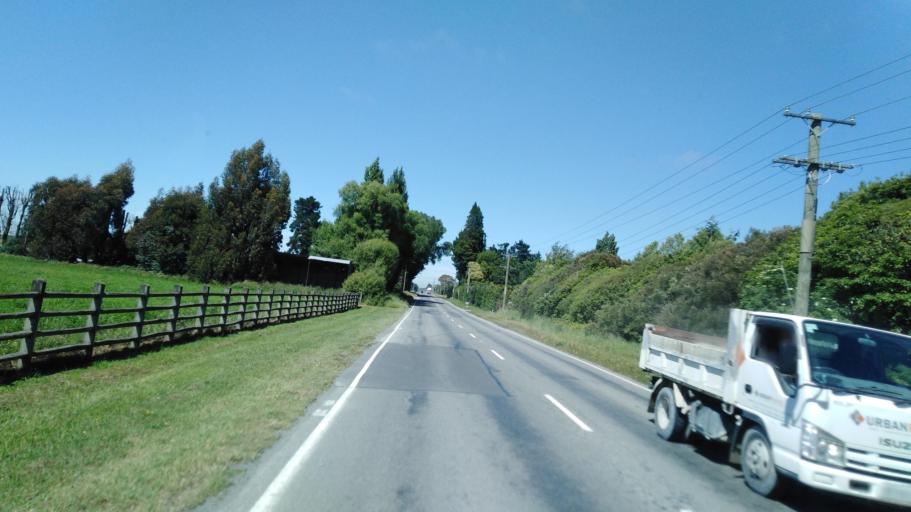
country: NZ
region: Canterbury
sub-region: Selwyn District
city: Prebbleton
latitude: -43.5228
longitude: 172.5030
